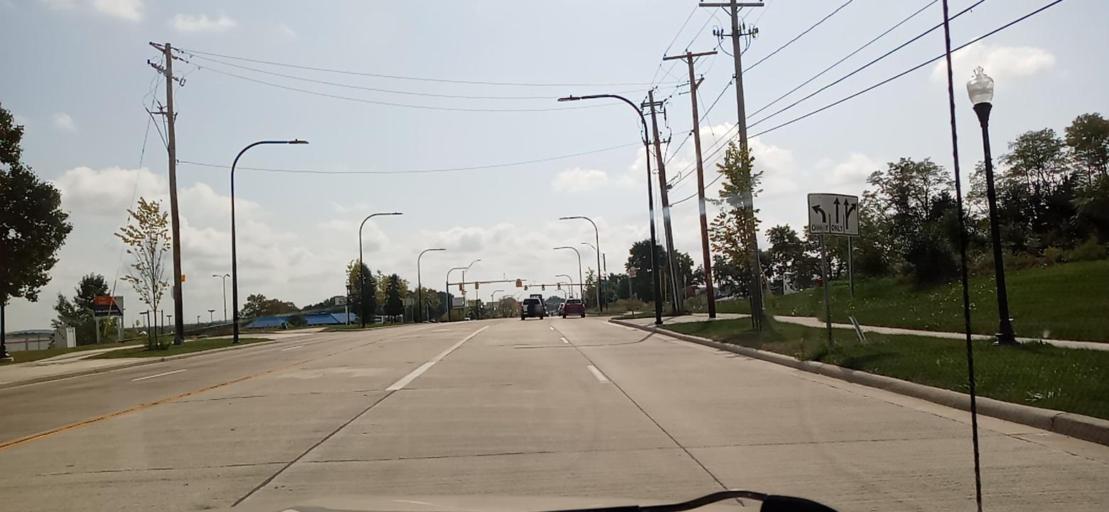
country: US
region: Ohio
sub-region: Summit County
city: Barberton
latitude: 41.0531
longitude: -81.5807
